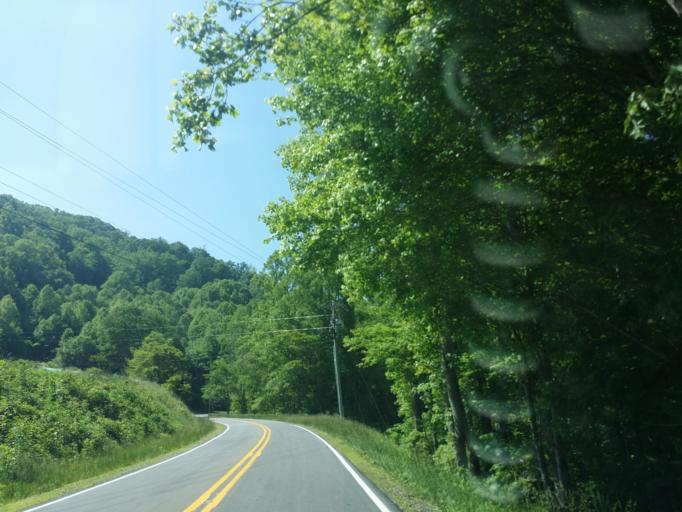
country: US
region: North Carolina
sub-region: Madison County
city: Marshall
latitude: 35.7394
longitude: -82.8408
